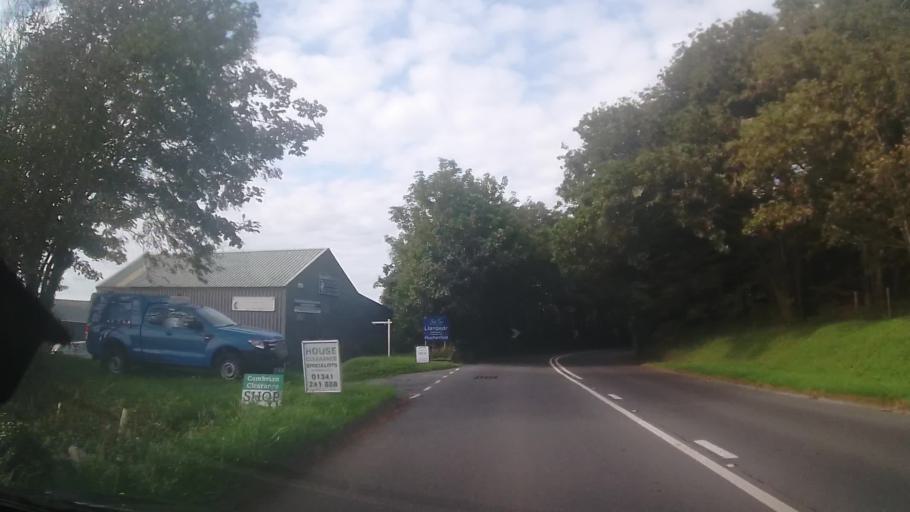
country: GB
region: Wales
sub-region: Gwynedd
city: Llanbedr
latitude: 52.8161
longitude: -4.1042
